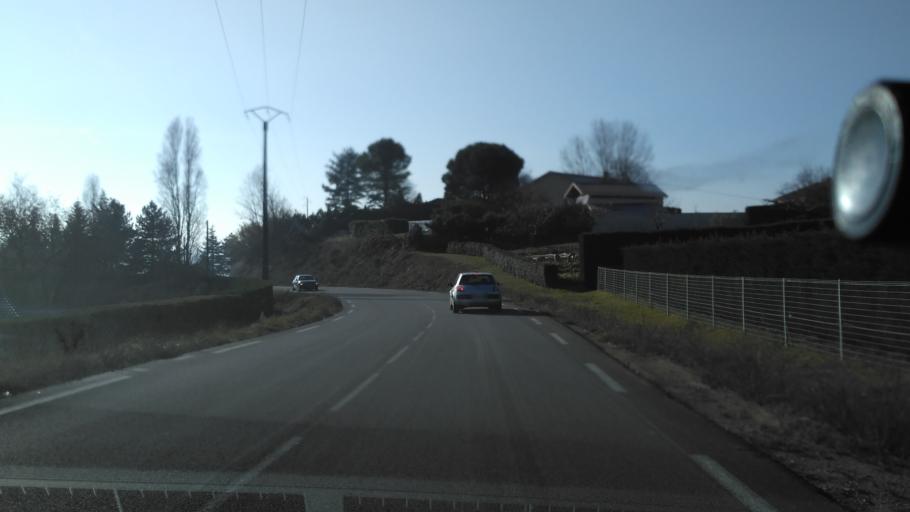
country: FR
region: Rhone-Alpes
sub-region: Departement de la Drome
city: Genissieux
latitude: 45.0967
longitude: 5.0910
